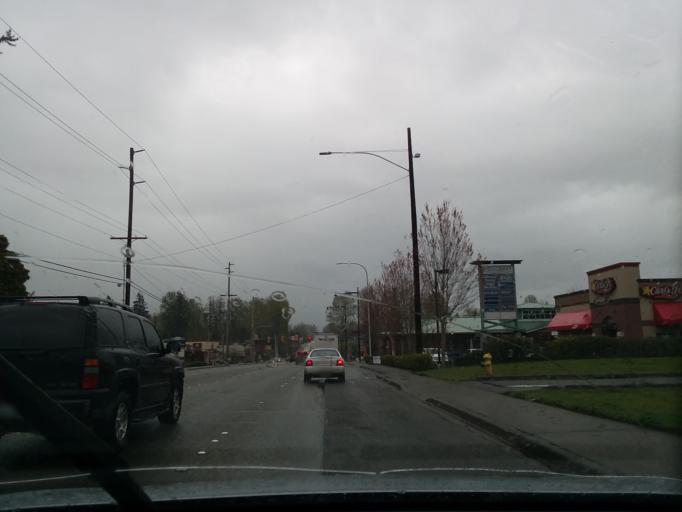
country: US
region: Washington
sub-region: King County
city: Fairwood
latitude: 47.4885
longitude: -122.1583
